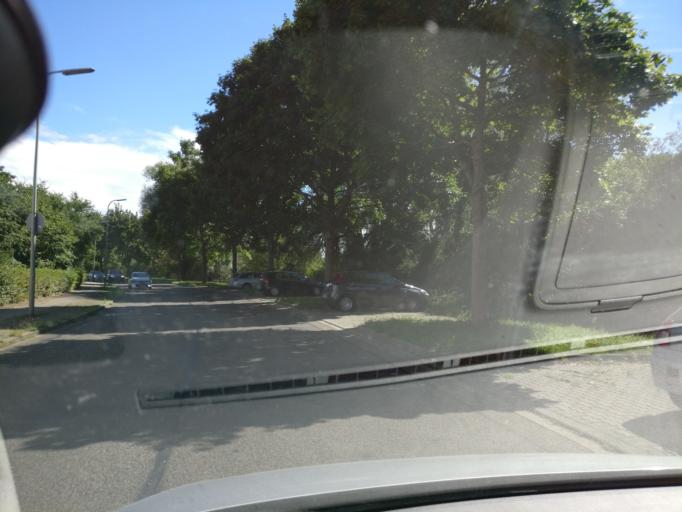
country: DE
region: Baden-Wuerttemberg
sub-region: Karlsruhe Region
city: Karlsruhe
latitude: 49.0229
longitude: 8.4532
